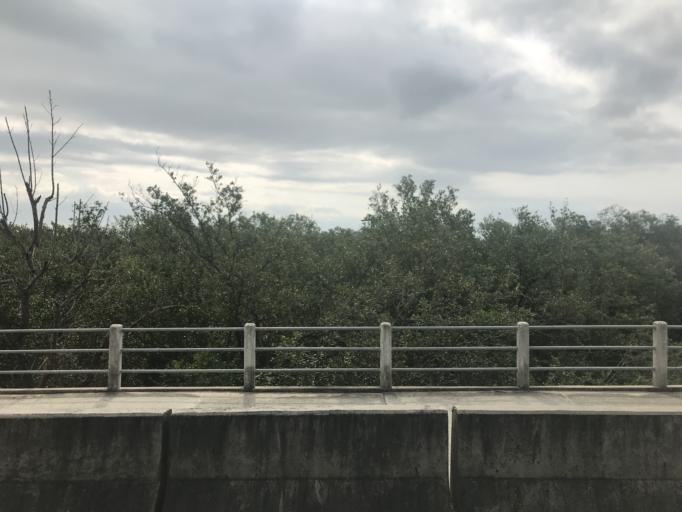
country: BR
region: Santa Catarina
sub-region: Florianopolis
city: Costeira do Pirajubae
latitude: -27.6516
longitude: -48.5231
